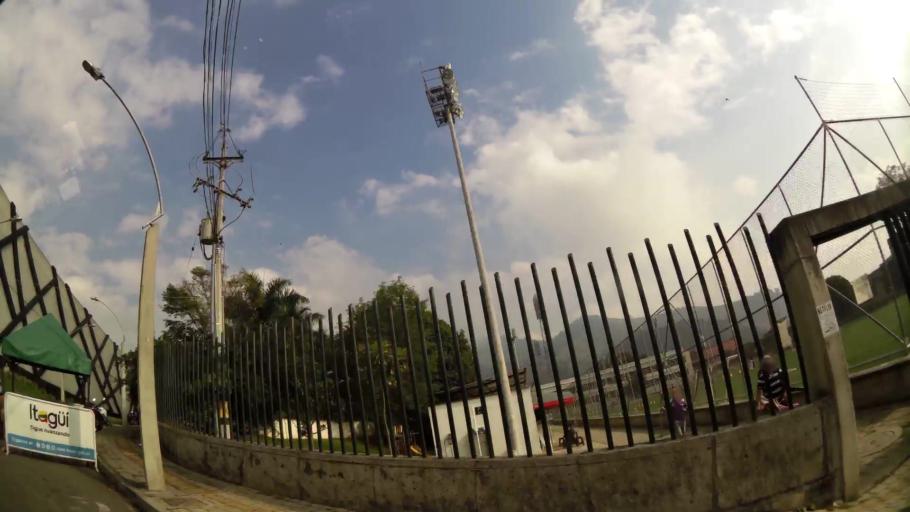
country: CO
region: Antioquia
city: Sabaneta
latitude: 6.1670
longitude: -75.6262
